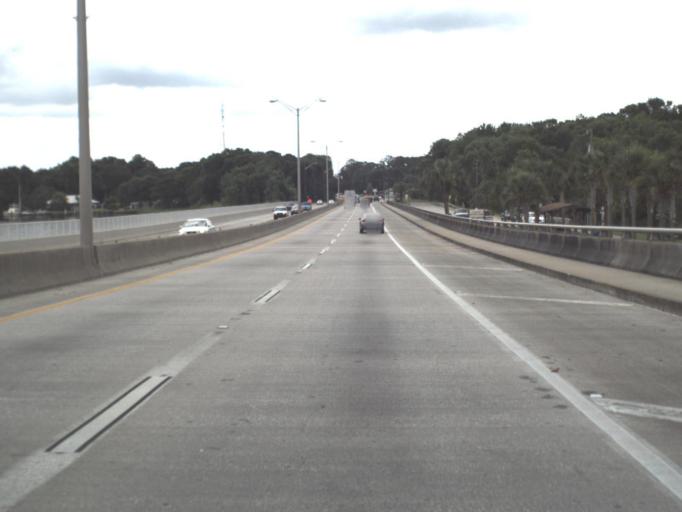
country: US
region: Florida
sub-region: Putnam County
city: Palatka
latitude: 29.6450
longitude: -81.6187
